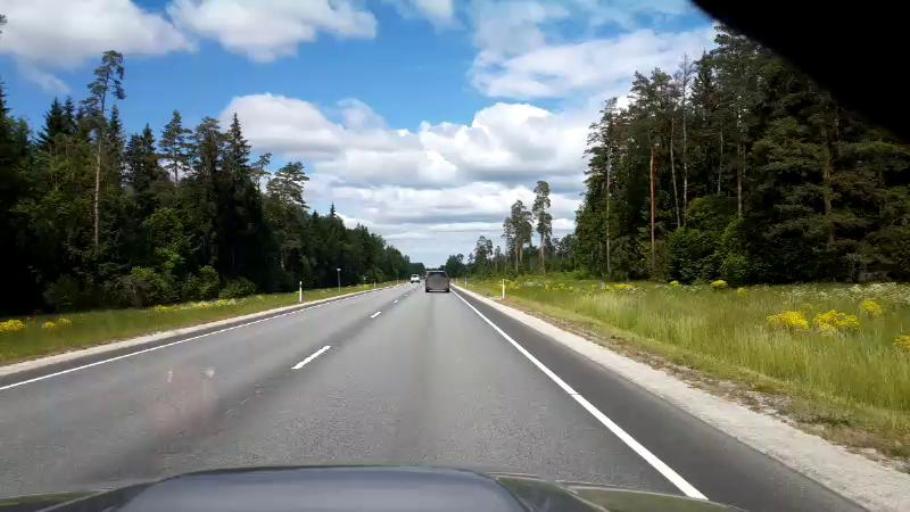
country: EE
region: Harju
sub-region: Nissi vald
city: Riisipere
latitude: 59.0929
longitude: 24.4649
